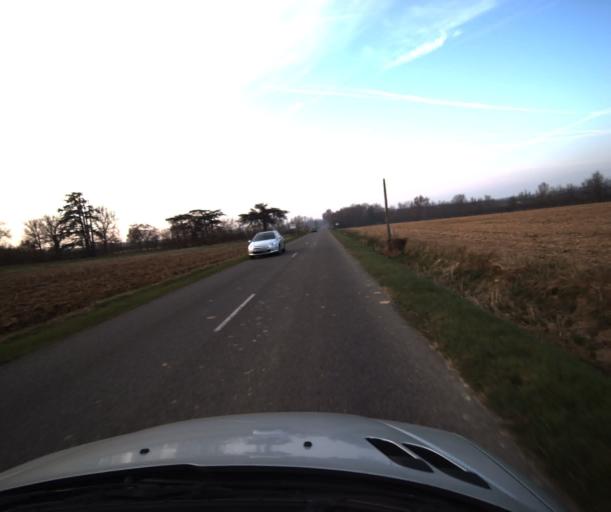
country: FR
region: Midi-Pyrenees
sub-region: Departement du Tarn-et-Garonne
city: Labastide-Saint-Pierre
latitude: 43.8962
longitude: 1.3716
